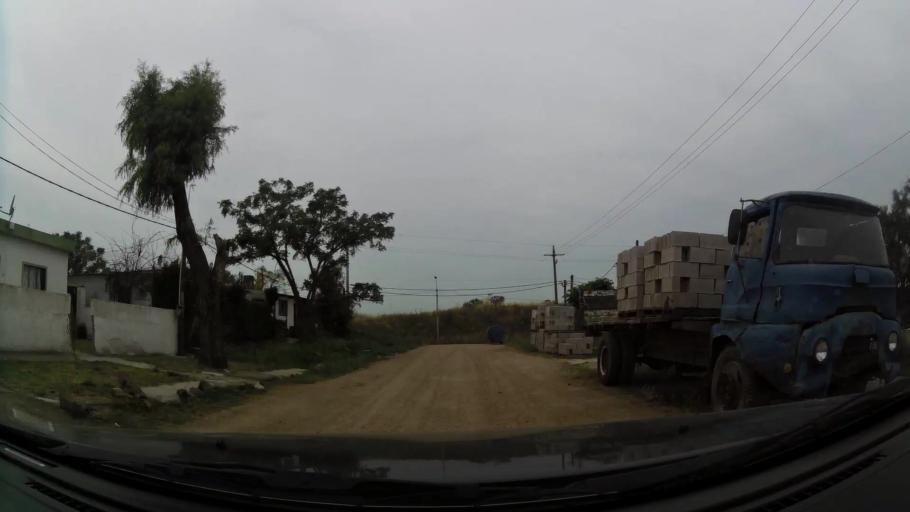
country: UY
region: Canelones
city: La Paz
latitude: -34.7464
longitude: -56.2414
